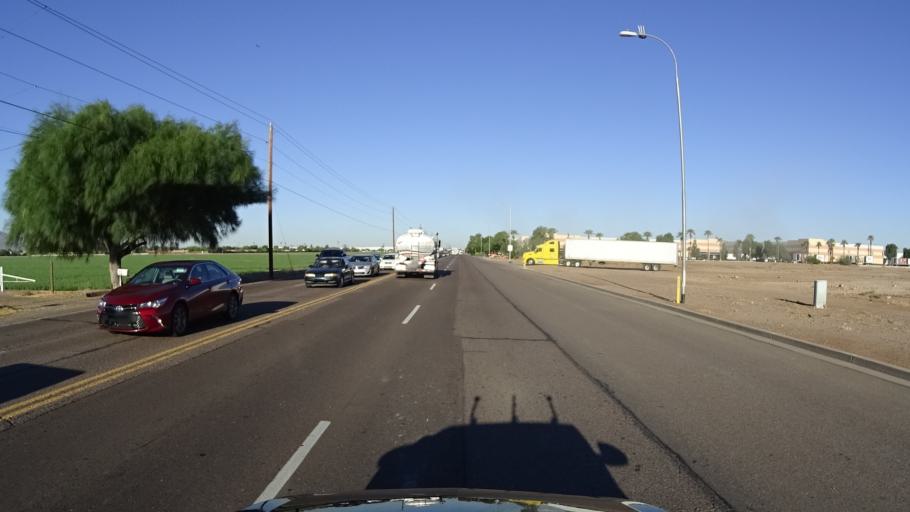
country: US
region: Arizona
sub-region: Maricopa County
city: Tolleson
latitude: 33.4371
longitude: -112.1913
